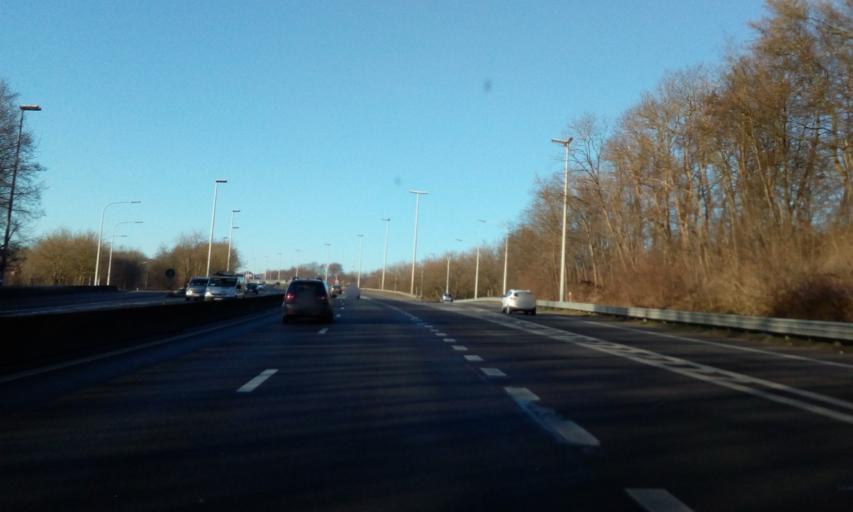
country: BE
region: Wallonia
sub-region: Province du Hainaut
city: Charleroi
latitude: 50.4348
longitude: 4.4509
